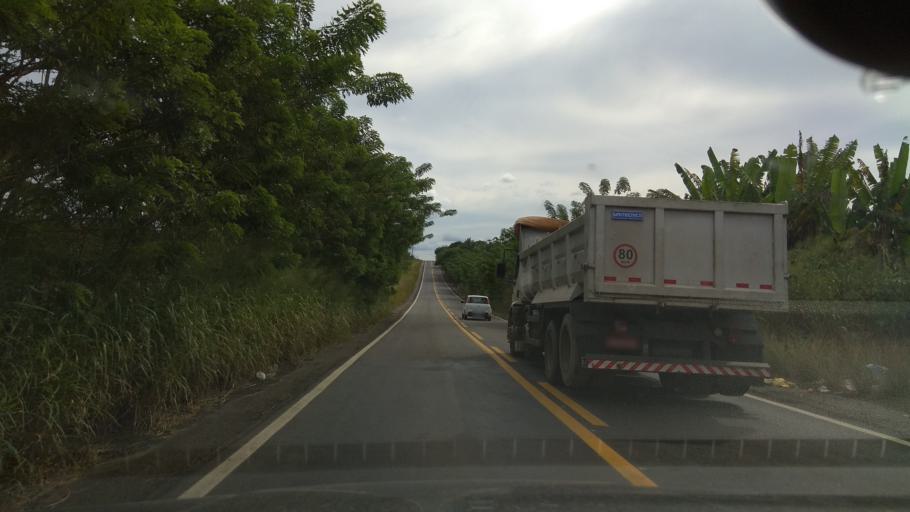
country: BR
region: Bahia
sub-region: Ubata
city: Ubata
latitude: -14.1969
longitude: -39.6205
